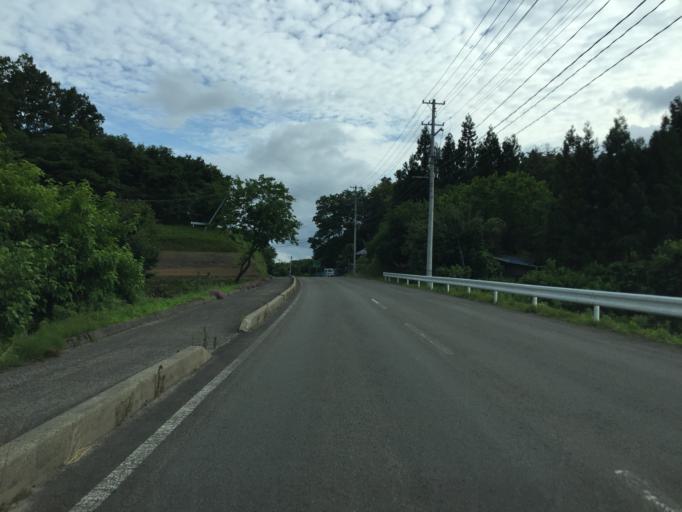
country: JP
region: Fukushima
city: Fukushima-shi
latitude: 37.6904
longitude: 140.5020
